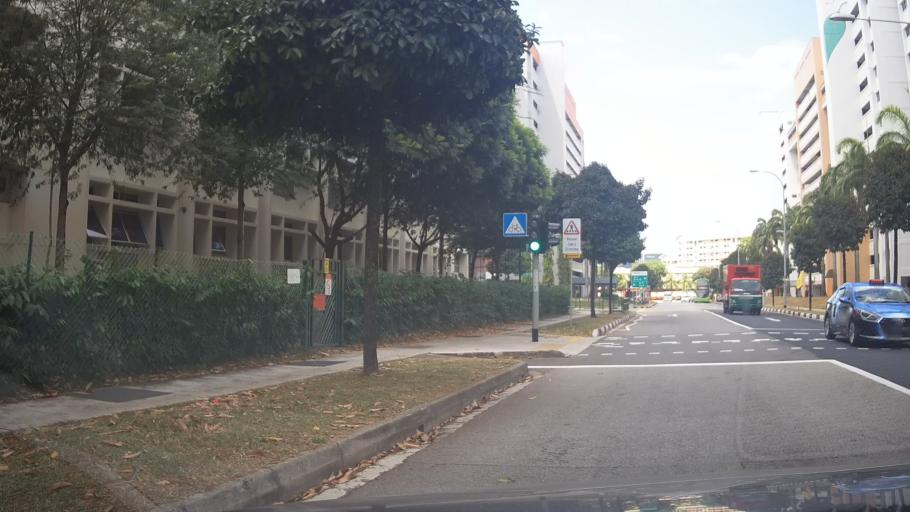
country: SG
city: Singapore
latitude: 1.3551
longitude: 103.9483
